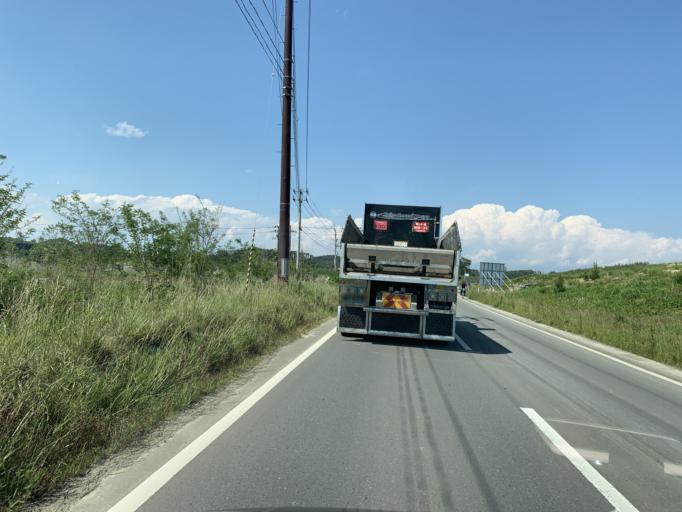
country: JP
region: Miyagi
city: Yamoto
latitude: 38.3646
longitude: 141.1573
